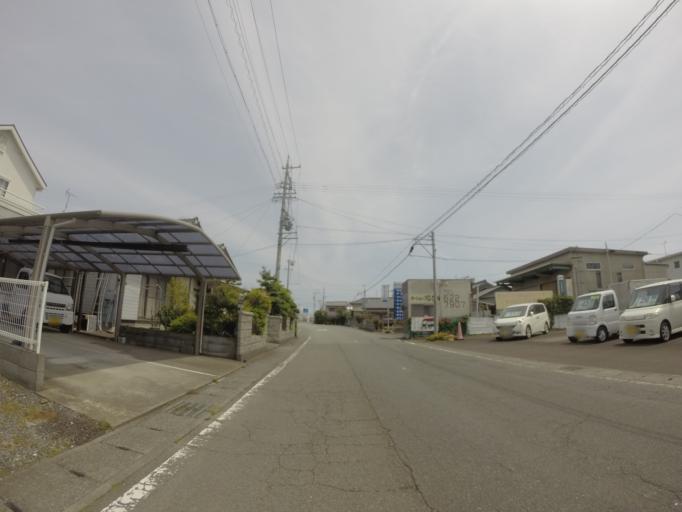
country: JP
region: Shizuoka
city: Yaizu
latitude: 34.7896
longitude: 138.3034
